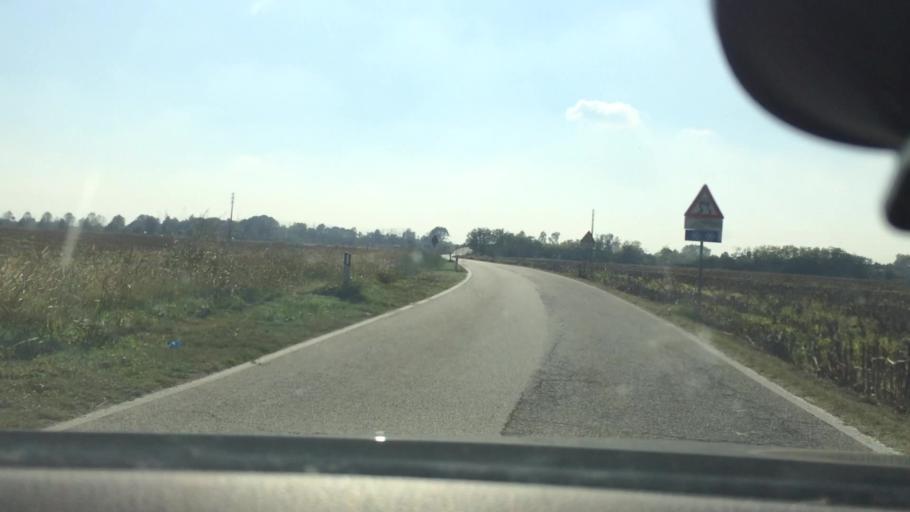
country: IT
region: Lombardy
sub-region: Citta metropolitana di Milano
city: Mesero
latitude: 45.4969
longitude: 8.8454
